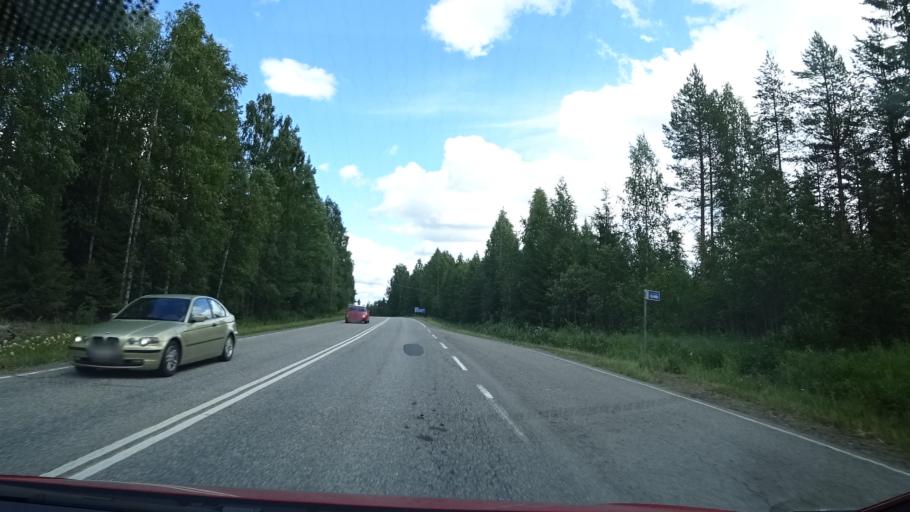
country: FI
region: Northern Savo
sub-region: Koillis-Savo
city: Juankoski
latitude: 63.2743
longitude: 28.3221
